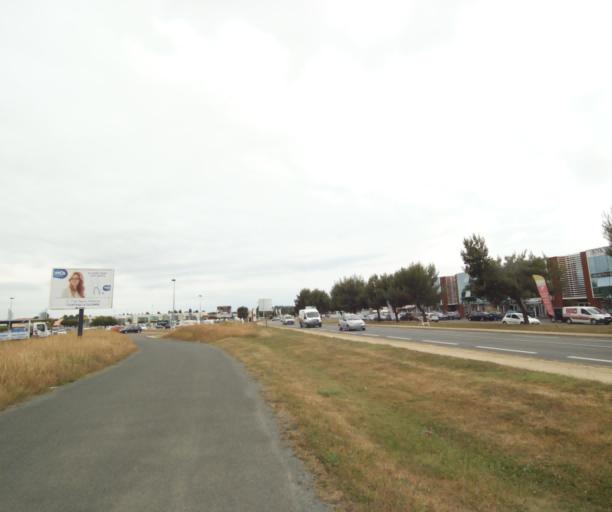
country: FR
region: Pays de la Loire
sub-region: Departement de la Vendee
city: Chateau-d'Olonne
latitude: 46.4947
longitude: -1.7513
